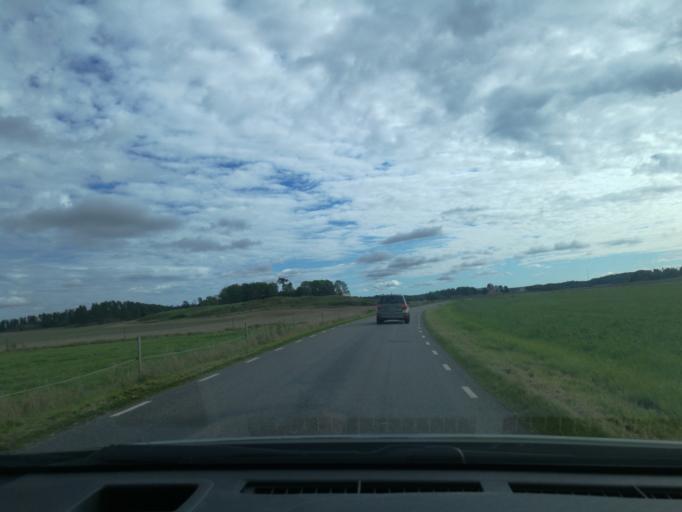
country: SE
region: OEstergoetland
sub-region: Soderkopings Kommun
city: Soederkoeping
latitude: 58.5049
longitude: 16.4567
